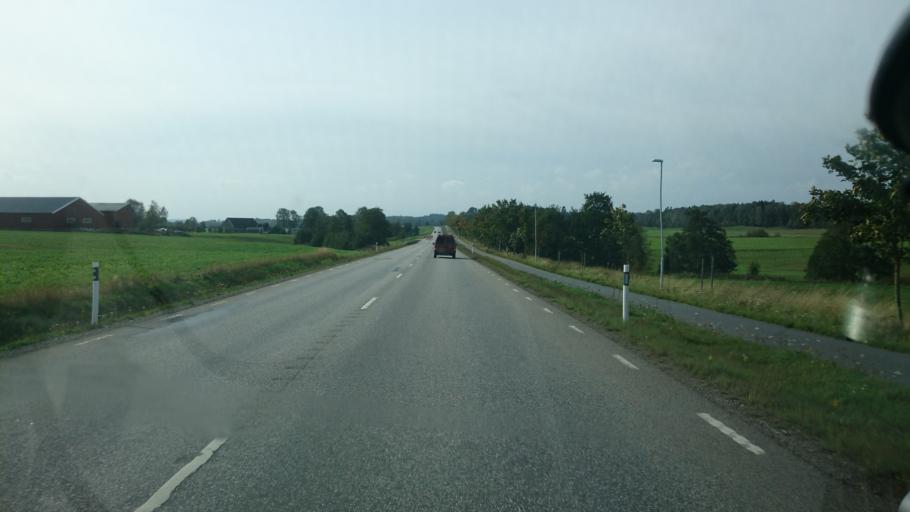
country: SE
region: Vaestra Goetaland
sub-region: Alingsas Kommun
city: Sollebrunn
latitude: 58.1003
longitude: 12.5091
